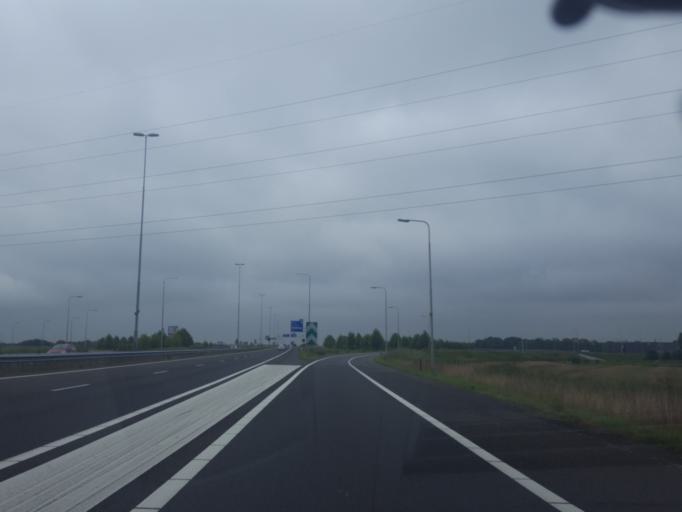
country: NL
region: Friesland
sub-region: Gemeente Heerenveen
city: Heerenveen
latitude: 52.9784
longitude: 5.9092
